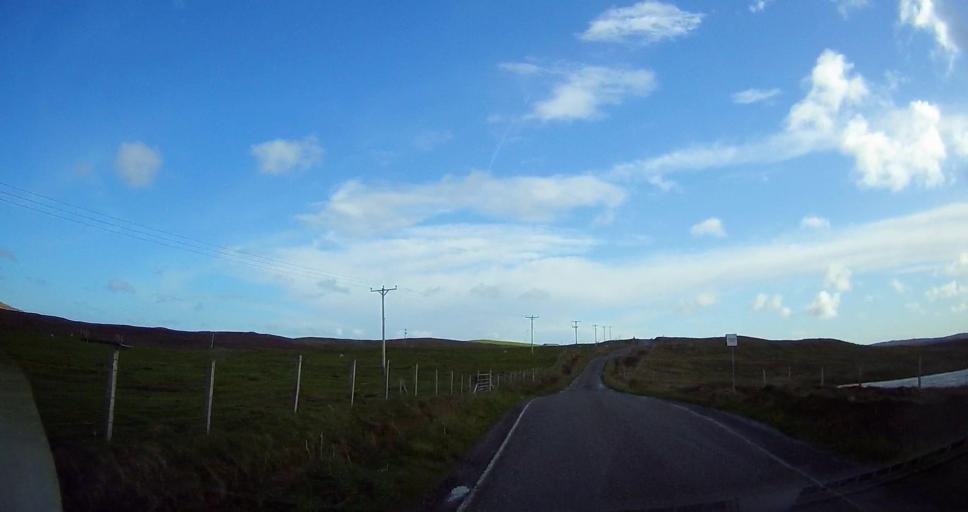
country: GB
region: Scotland
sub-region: Shetland Islands
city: Shetland
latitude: 60.3656
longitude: -1.1416
